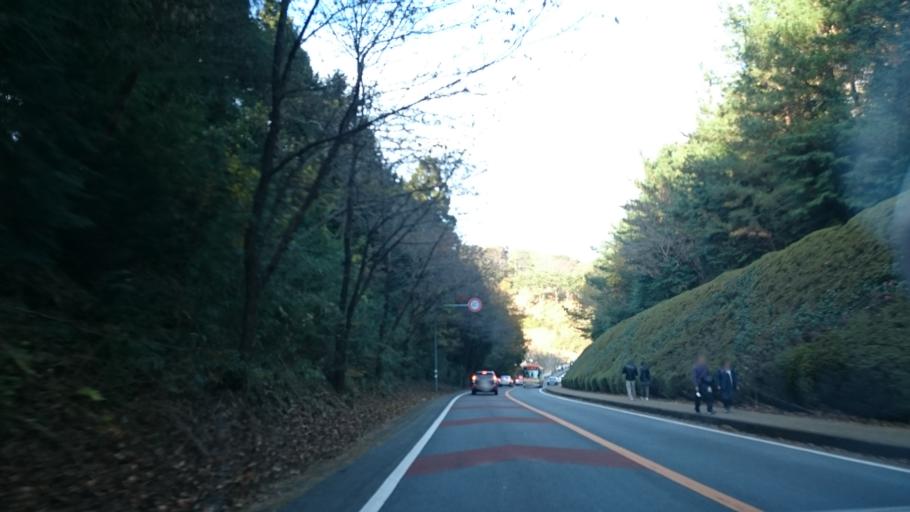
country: JP
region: Shizuoka
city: Heda
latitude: 34.9745
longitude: 138.9138
